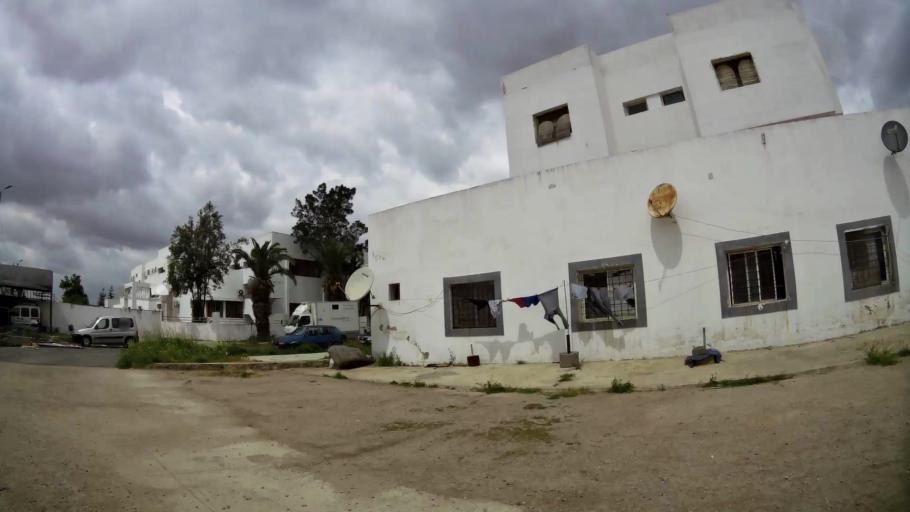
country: MA
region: Grand Casablanca
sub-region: Casablanca
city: Casablanca
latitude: 33.5596
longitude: -7.6100
